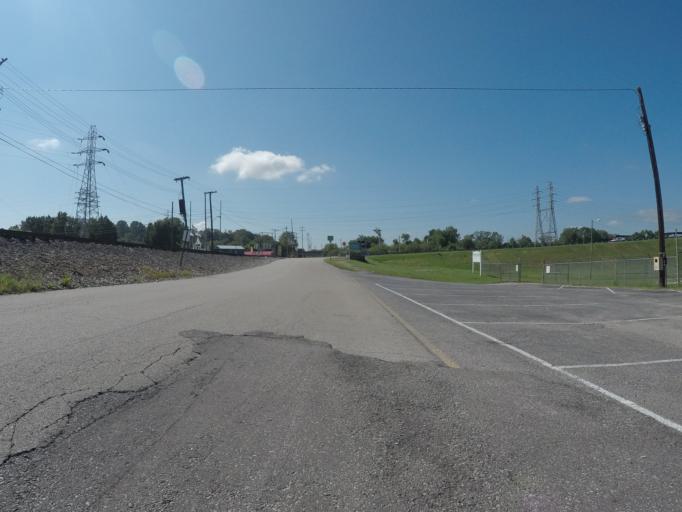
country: US
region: Kentucky
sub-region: Boyd County
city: Catlettsburg
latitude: 38.4041
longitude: -82.5908
